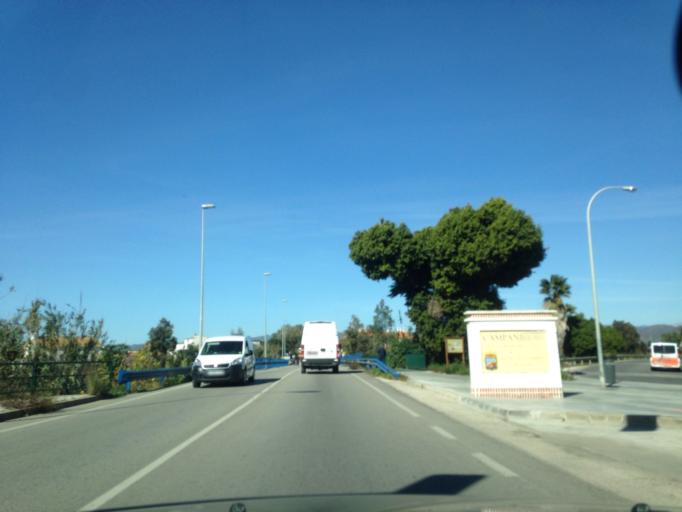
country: ES
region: Andalusia
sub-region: Provincia de Malaga
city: Alhaurin de la Torre
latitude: 36.7209
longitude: -4.5351
